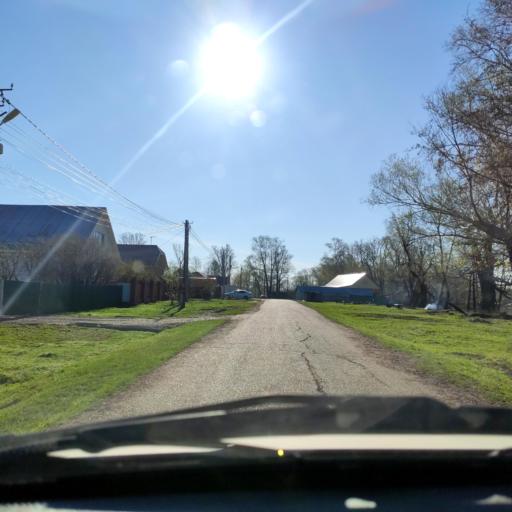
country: RU
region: Bashkortostan
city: Mikhaylovka
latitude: 54.7779
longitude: 55.8309
